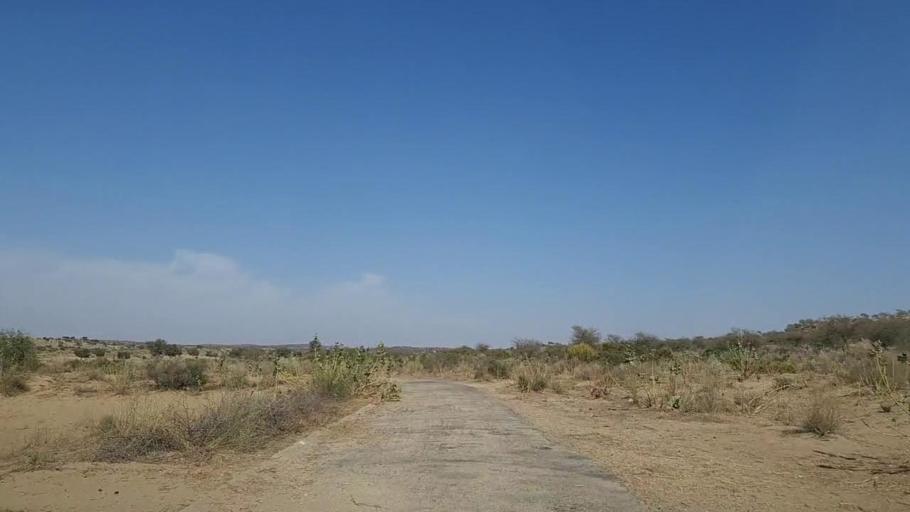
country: PK
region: Sindh
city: Nabisar
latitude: 24.8726
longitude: 69.6094
